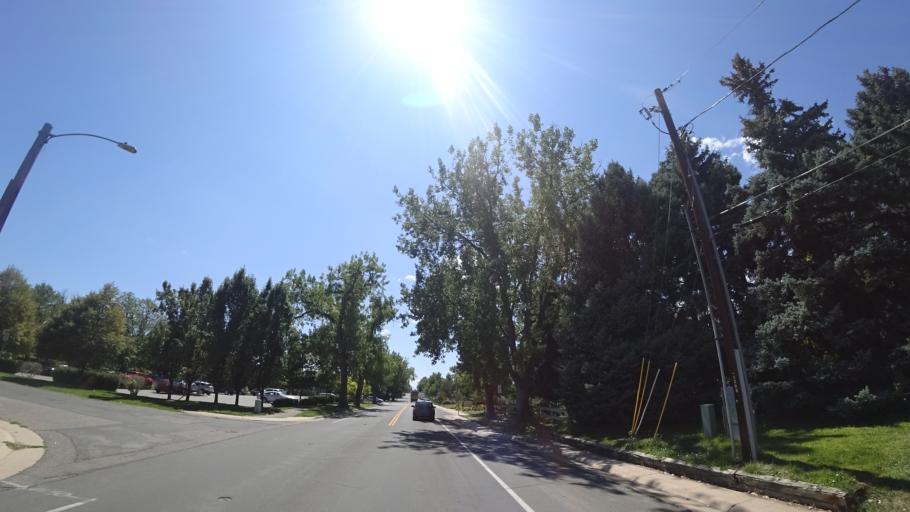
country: US
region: Colorado
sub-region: Arapahoe County
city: Littleton
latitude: 39.6080
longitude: -105.0021
